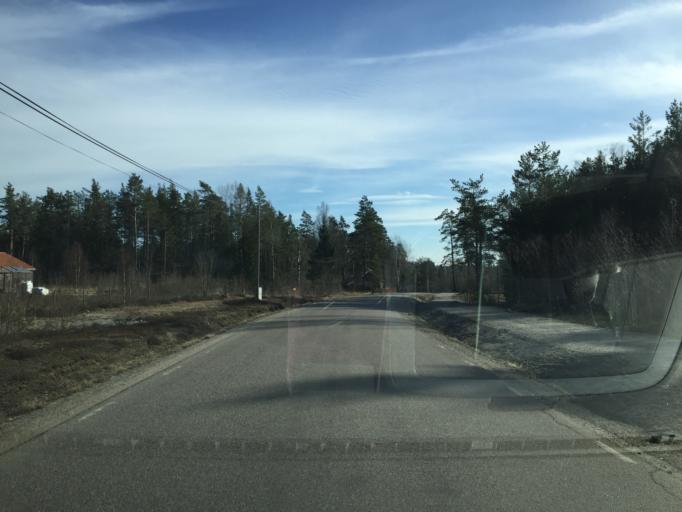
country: SE
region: Stockholm
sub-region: Nynashamns Kommun
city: Osmo
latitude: 59.0576
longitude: 17.8709
